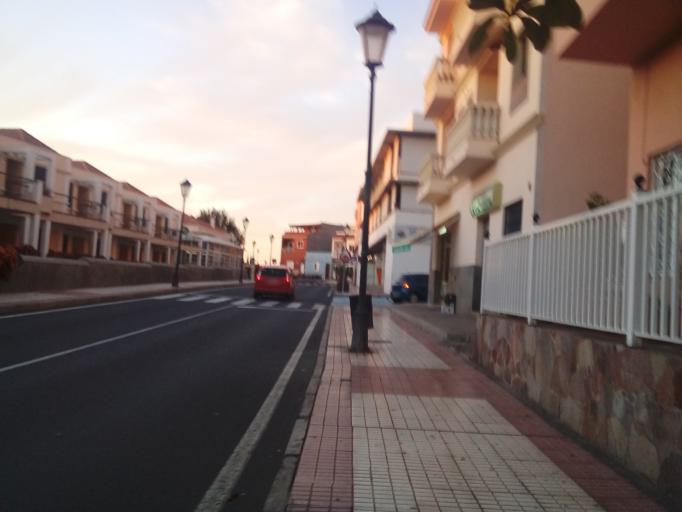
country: ES
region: Canary Islands
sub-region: Provincia de Santa Cruz de Tenerife
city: Alajero
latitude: 28.0877
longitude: -17.3353
